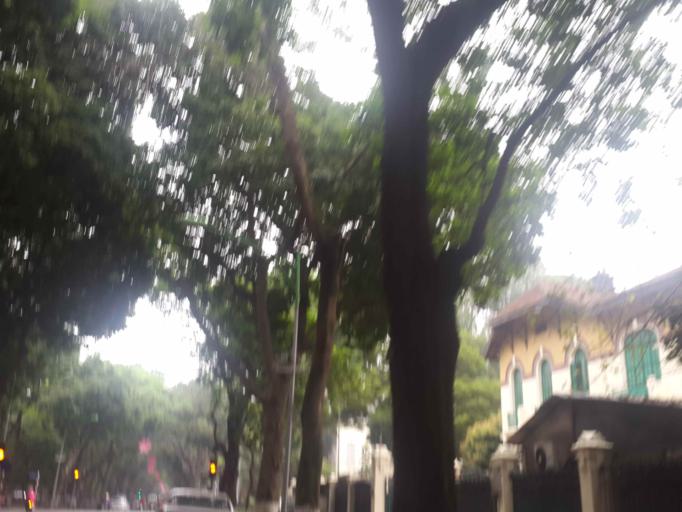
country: VN
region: Ha Noi
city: Hanoi
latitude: 21.0411
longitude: 105.8394
